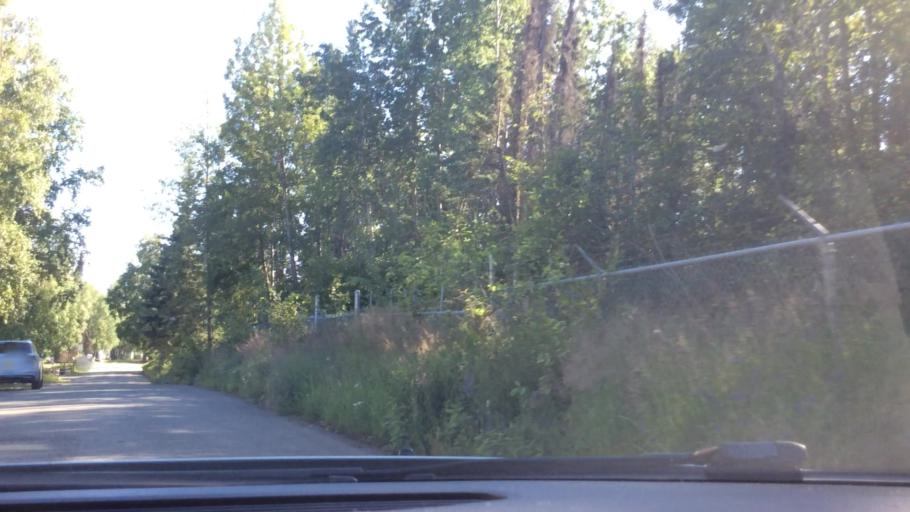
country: US
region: Alaska
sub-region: Anchorage Municipality
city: Anchorage
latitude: 61.1536
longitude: -149.8363
